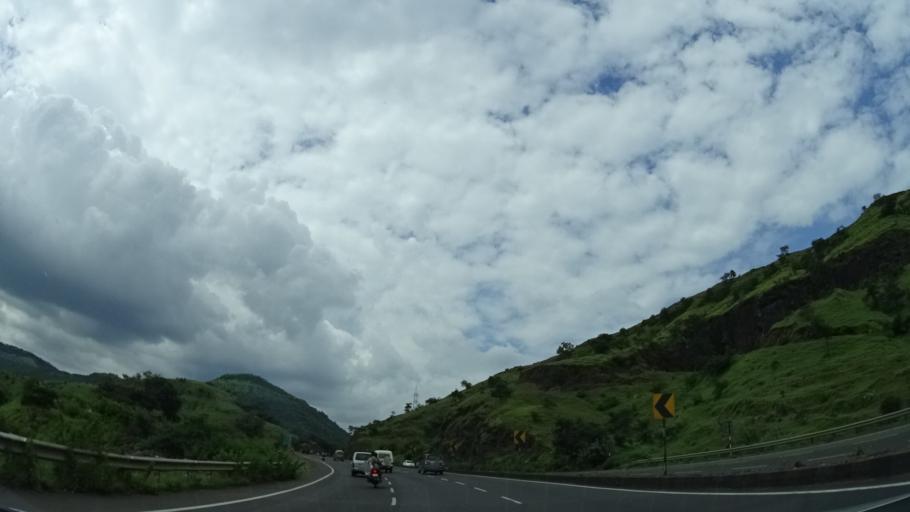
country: IN
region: Maharashtra
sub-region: Satara Division
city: Satara
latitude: 17.6511
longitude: 74.0139
